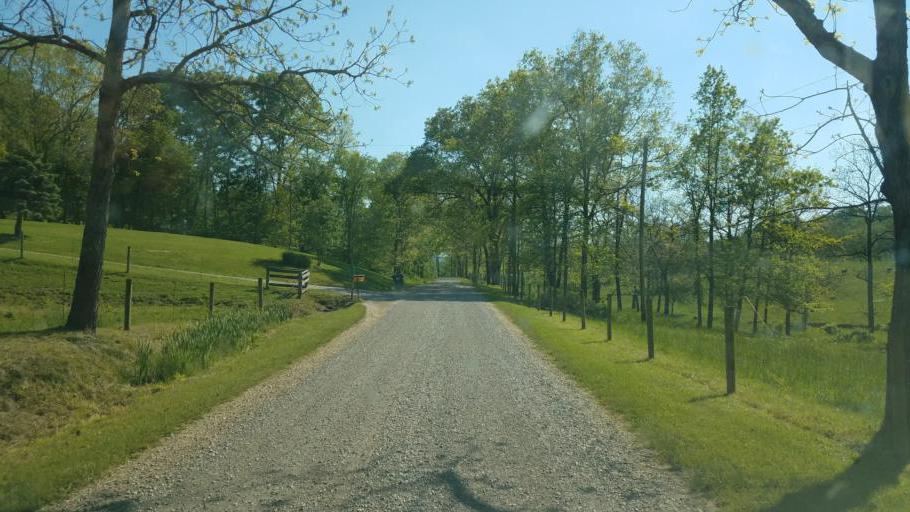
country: US
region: Ohio
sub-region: Belmont County
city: Barnesville
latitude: 40.0644
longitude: -81.3352
